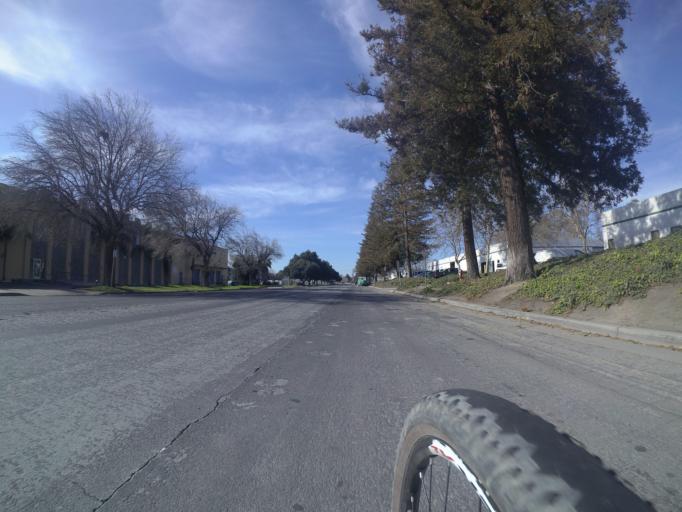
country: US
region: California
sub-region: Santa Clara County
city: Milpitas
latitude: 37.3930
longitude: -121.9137
